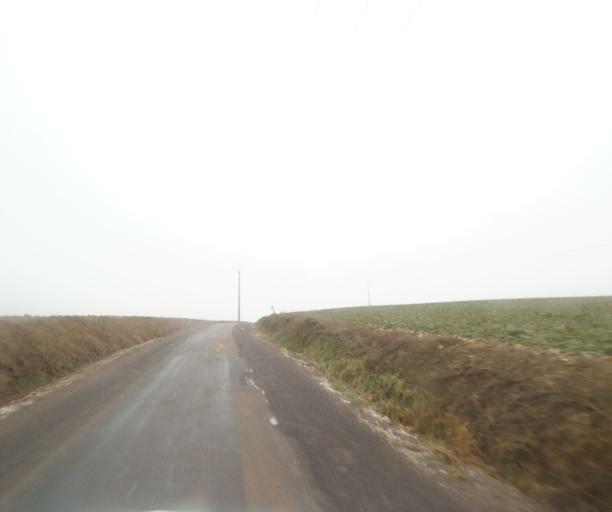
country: FR
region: Champagne-Ardenne
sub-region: Departement de la Haute-Marne
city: Bienville
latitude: 48.5407
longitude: 5.0649
